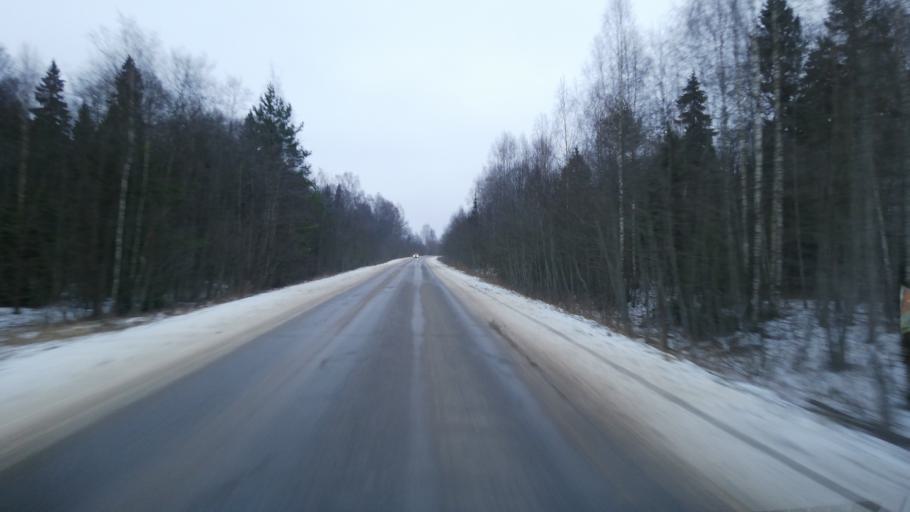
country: RU
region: Kostroma
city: Oktyabr'skiy
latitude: 57.7171
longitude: 41.1315
